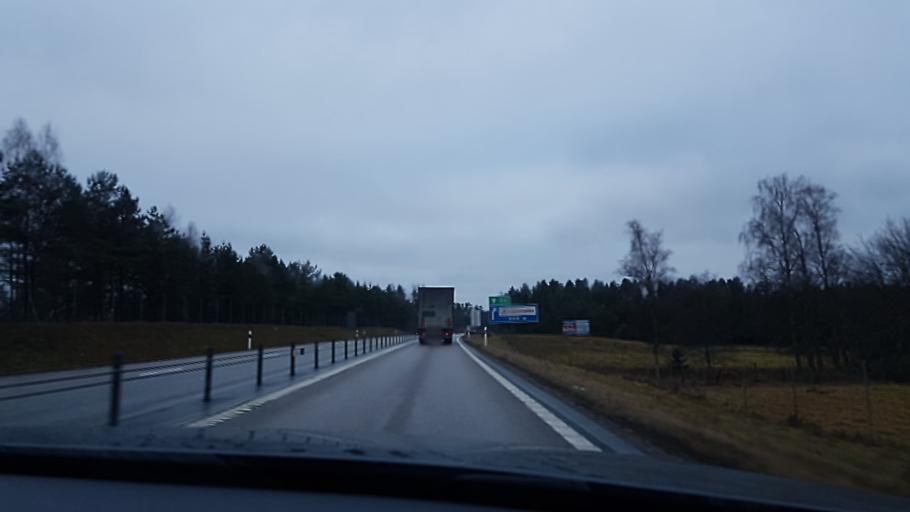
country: SE
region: Kronoberg
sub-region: Ljungby Kommun
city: Lagan
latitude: 56.9455
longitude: 13.9994
